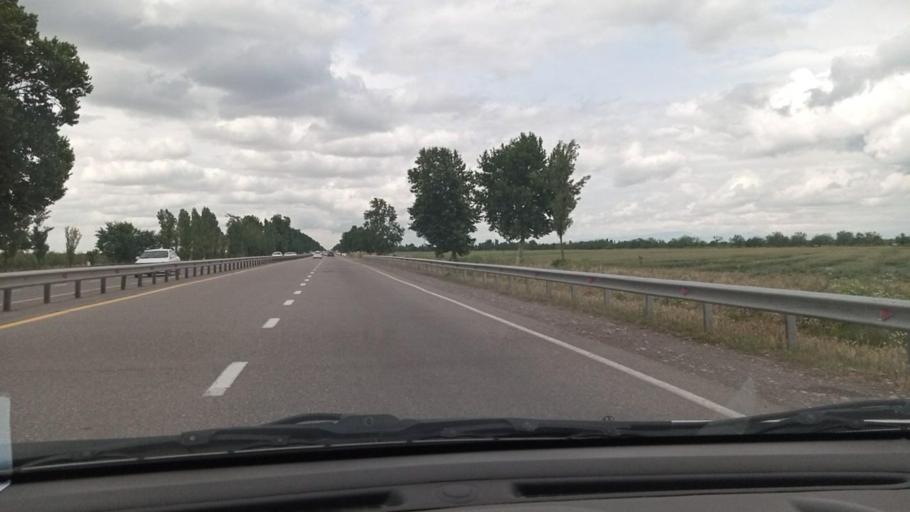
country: UZ
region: Toshkent Shahri
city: Bektemir
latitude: 41.1952
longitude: 69.4032
